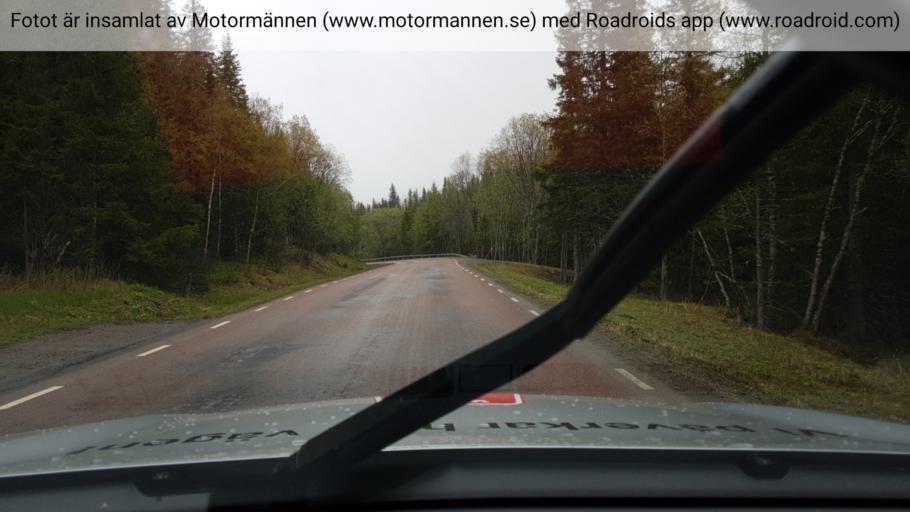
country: SE
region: Jaemtland
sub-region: Are Kommun
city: Jarpen
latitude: 63.1044
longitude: 13.8329
